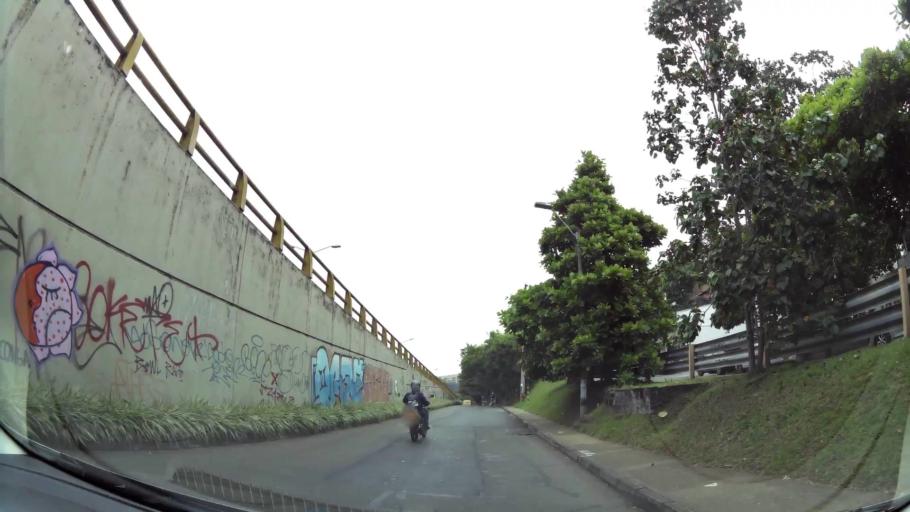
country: CO
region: Antioquia
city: Itagui
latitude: 6.1959
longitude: -75.5789
